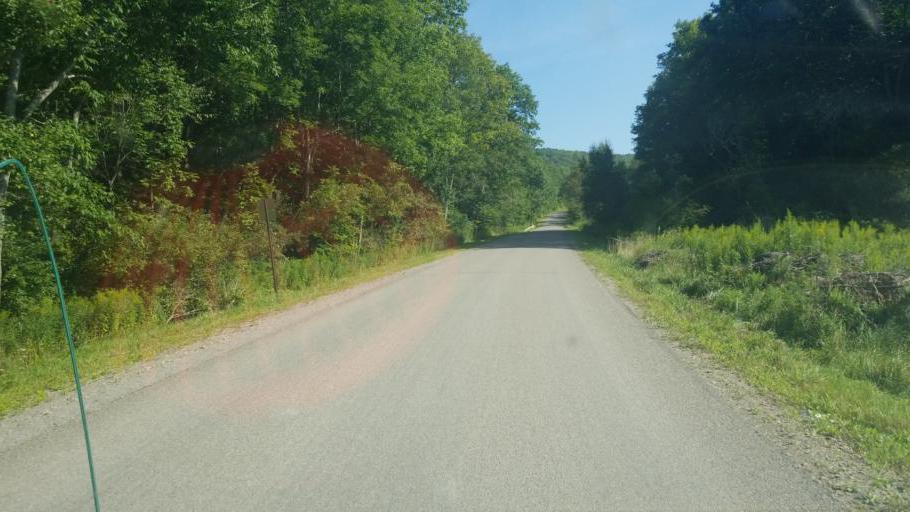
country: US
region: New York
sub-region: Allegany County
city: Wellsville
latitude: 42.0282
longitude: -77.9384
